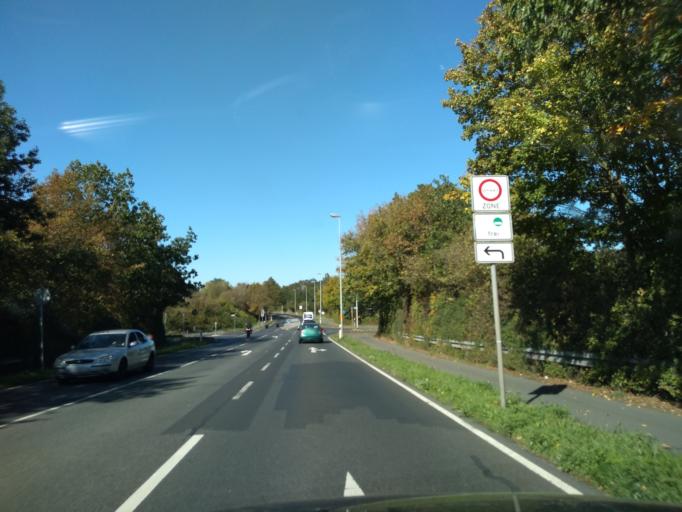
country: DE
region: North Rhine-Westphalia
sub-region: Regierungsbezirk Dusseldorf
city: Dinslaken
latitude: 51.5486
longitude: 6.7560
